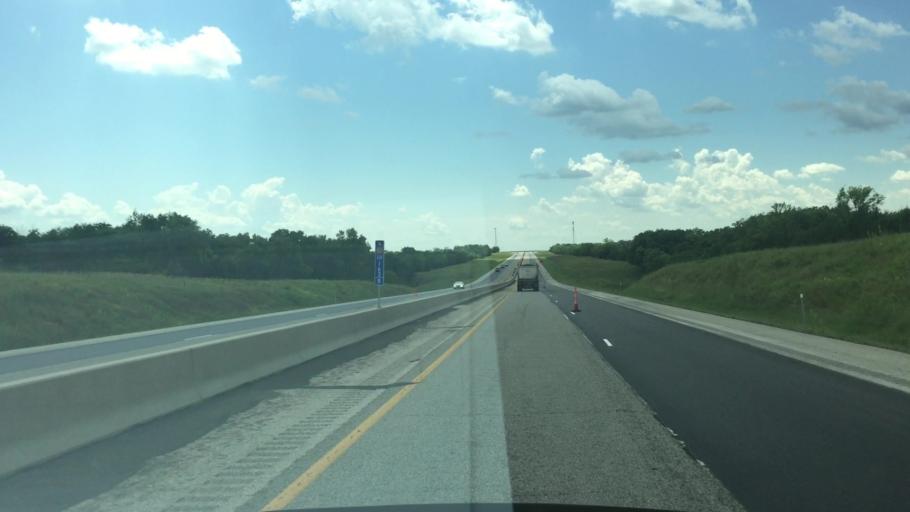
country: US
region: Kansas
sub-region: Shawnee County
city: Auburn
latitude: 38.8539
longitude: -95.8588
